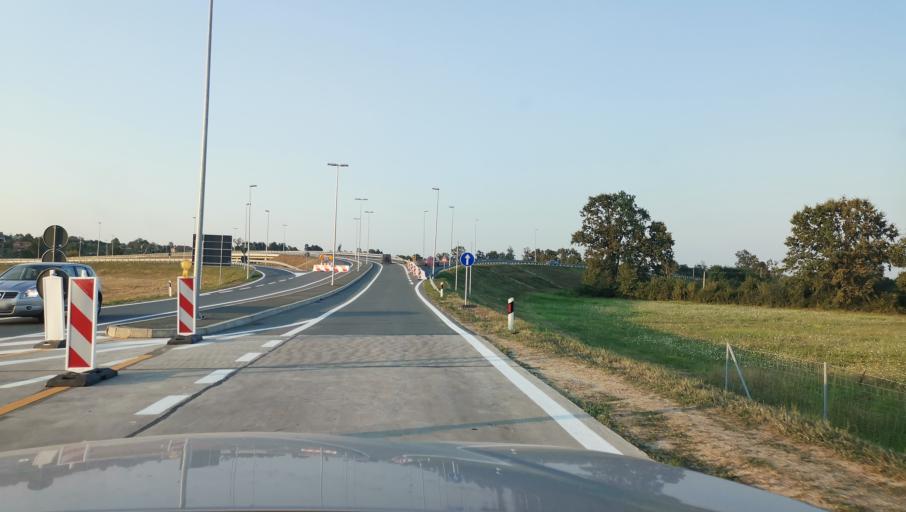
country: RS
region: Central Serbia
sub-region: Kolubarski Okrug
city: Lajkovac
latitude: 44.3602
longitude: 20.1313
